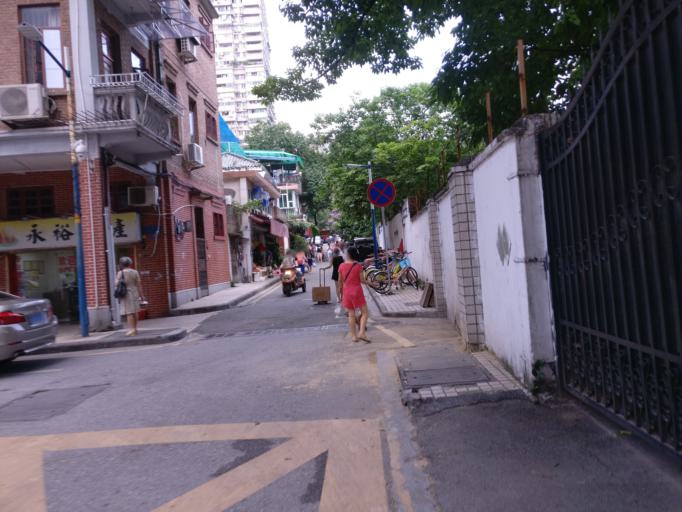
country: CN
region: Guangdong
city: Guangzhou
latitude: 23.1219
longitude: 113.2897
